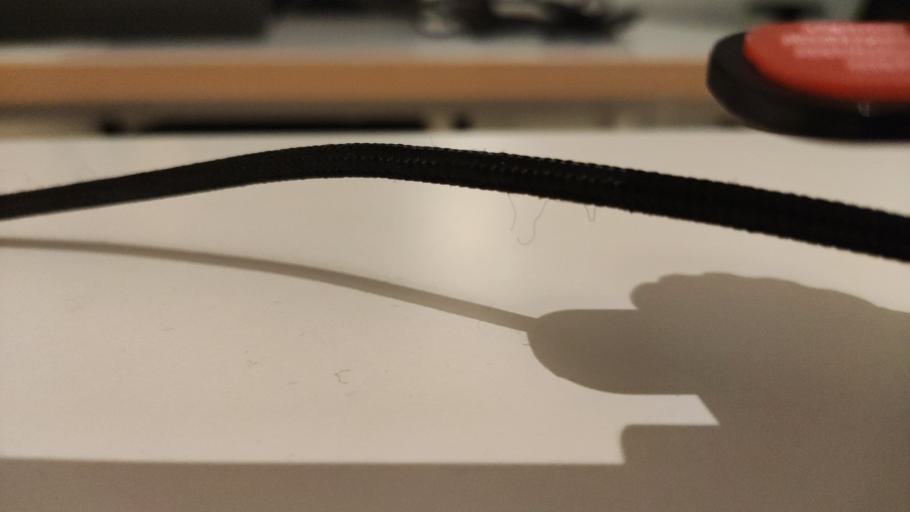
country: RU
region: Moskovskaya
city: Il'inskiy Pogost
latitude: 55.5150
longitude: 38.8715
